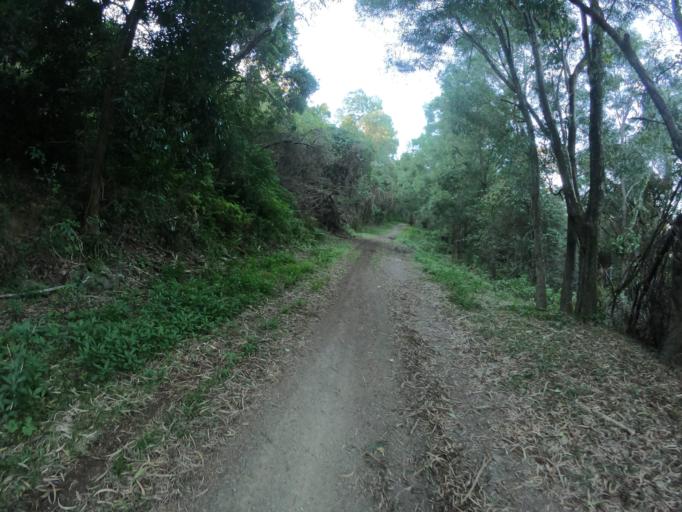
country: AU
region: New South Wales
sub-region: Wollongong
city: Mount Keira
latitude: -34.4109
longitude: 150.8328
